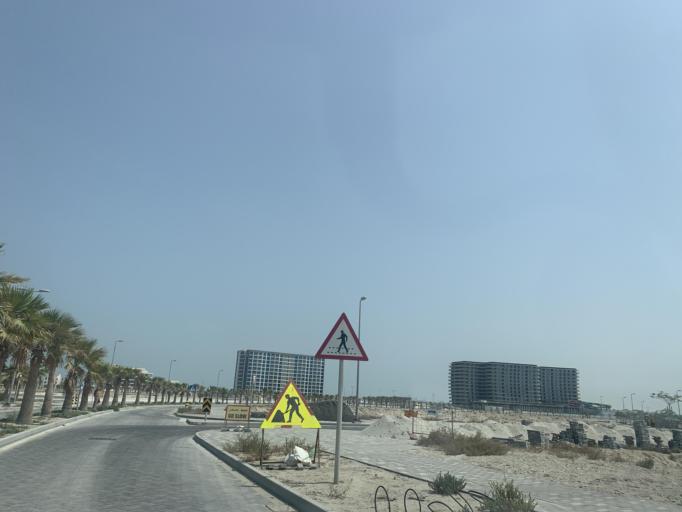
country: BH
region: Muharraq
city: Al Hadd
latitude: 26.2740
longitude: 50.6753
